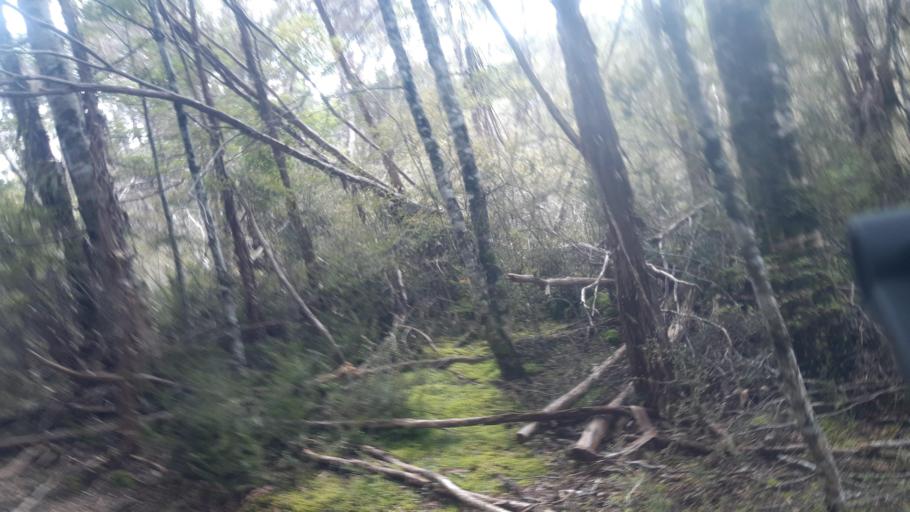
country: NZ
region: Tasman
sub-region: Tasman District
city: Wakefield
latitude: -41.7801
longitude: 172.8164
